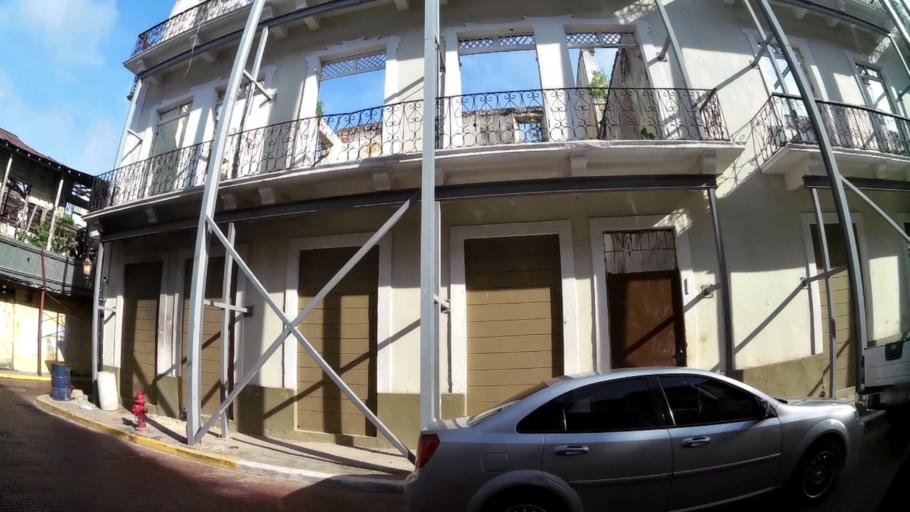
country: PA
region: Panama
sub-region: Distrito de Panama
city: Ancon
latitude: 8.9516
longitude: -79.5358
